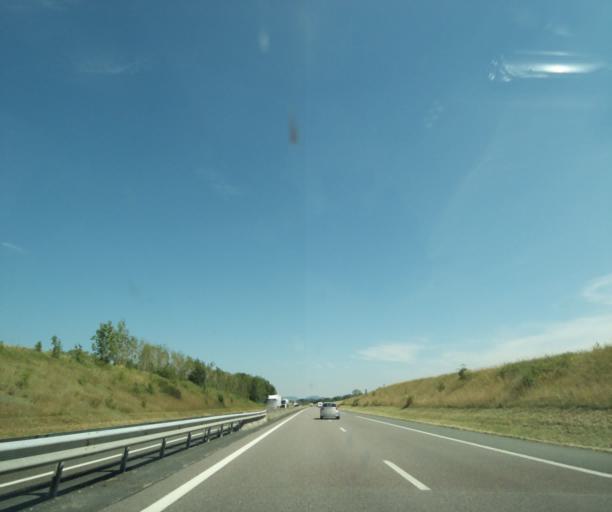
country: FR
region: Lorraine
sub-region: Departement de Meurthe-et-Moselle
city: Colombey-les-Belles
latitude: 48.5558
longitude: 5.8918
